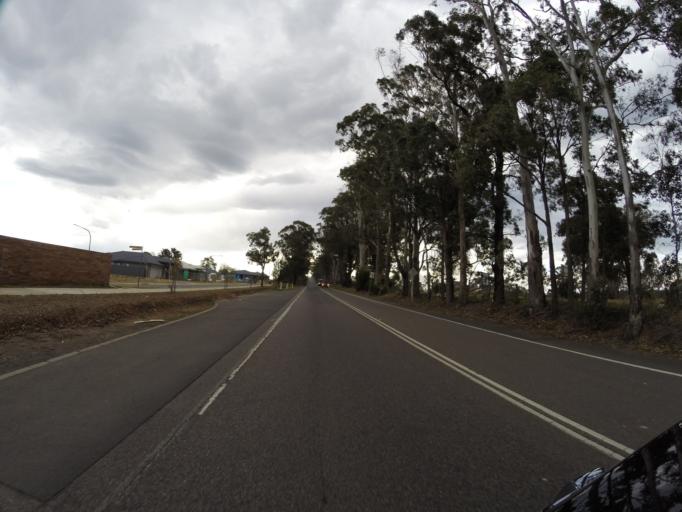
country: AU
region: New South Wales
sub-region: Wollondilly
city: Douglas Park
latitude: -34.1932
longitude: 150.7900
